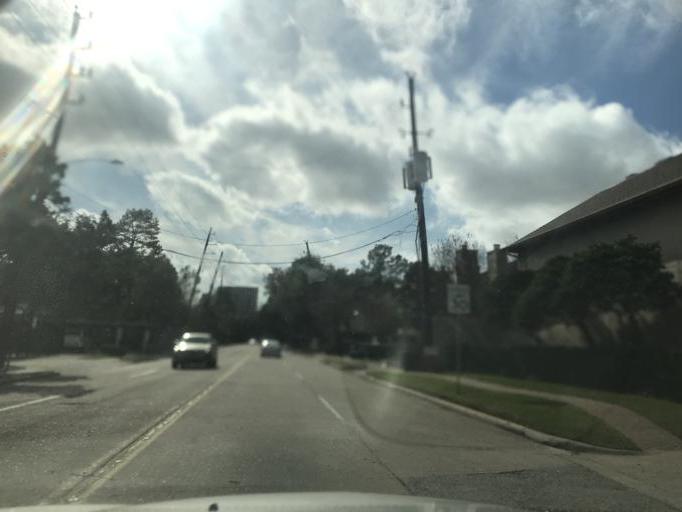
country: US
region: Texas
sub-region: Harris County
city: Hunters Creek Village
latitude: 29.7461
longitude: -95.4826
